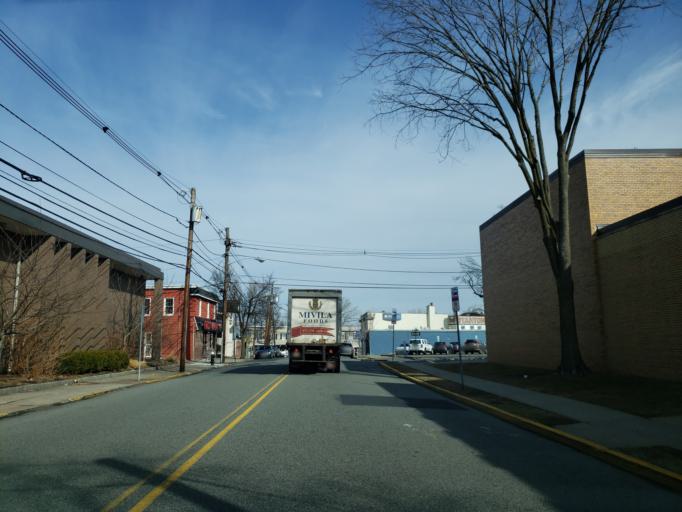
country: US
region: New Jersey
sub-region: Passaic County
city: Singac
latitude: 40.8804
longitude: -74.2289
